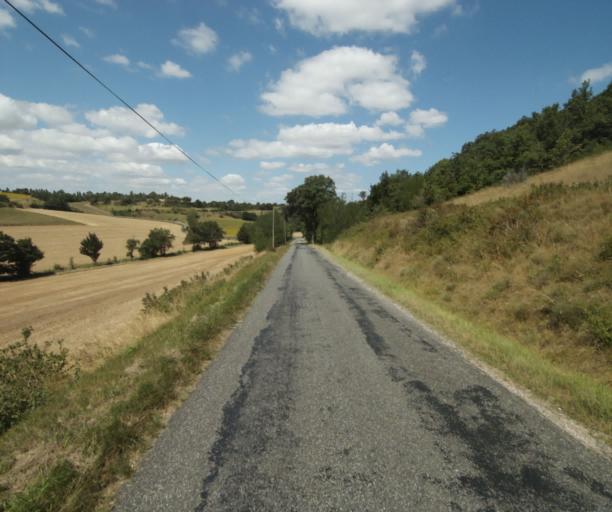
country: FR
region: Midi-Pyrenees
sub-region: Departement de la Haute-Garonne
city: Saint-Felix-Lauragais
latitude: 43.4682
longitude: 1.8512
